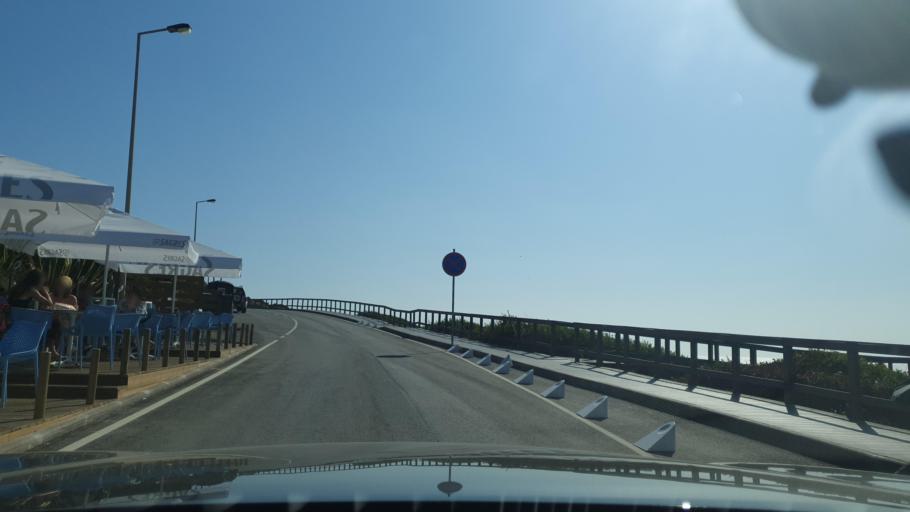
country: PT
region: Beja
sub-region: Odemira
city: Sao Teotonio
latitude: 37.4406
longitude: -8.7985
